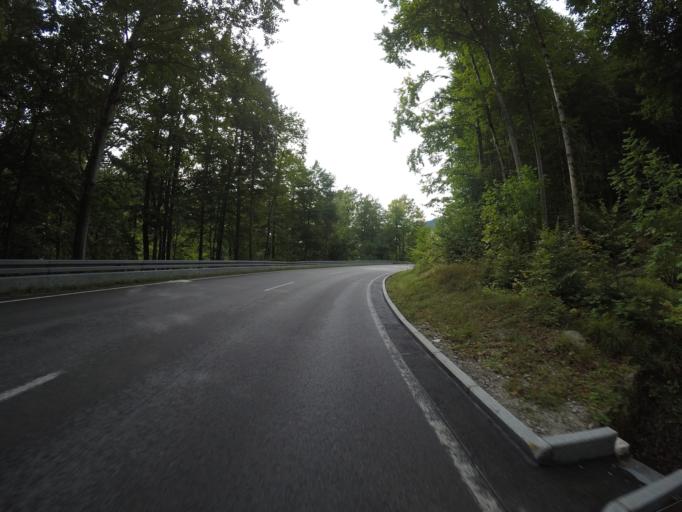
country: DE
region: Bavaria
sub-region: Upper Bavaria
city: Lenggries
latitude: 47.5808
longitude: 11.5474
